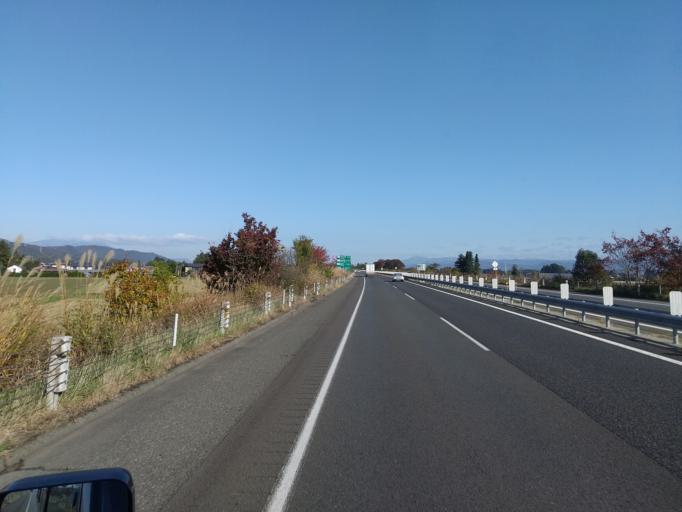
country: JP
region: Iwate
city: Morioka-shi
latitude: 39.5640
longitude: 141.1189
